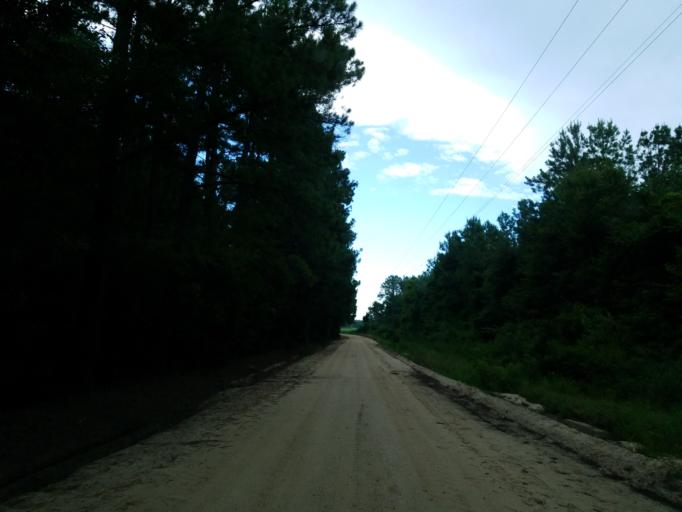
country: US
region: Georgia
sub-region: Tift County
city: Omega
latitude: 31.2628
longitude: -83.5318
